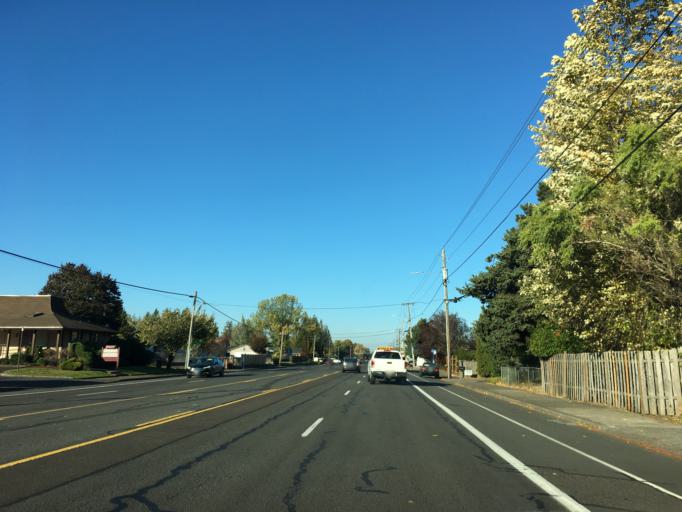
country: US
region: Oregon
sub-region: Multnomah County
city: Gresham
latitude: 45.5049
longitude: -122.4073
